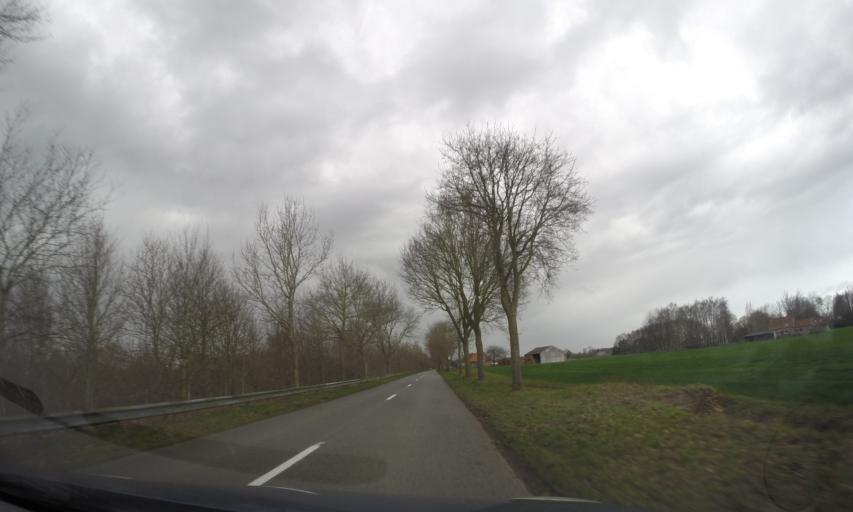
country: BE
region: Flanders
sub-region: Provincie West-Vlaanderen
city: Beernem
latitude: 51.1322
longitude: 3.3526
